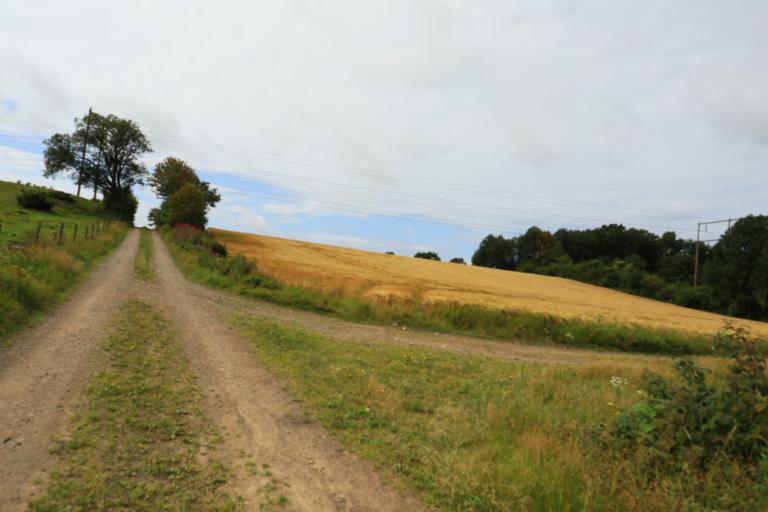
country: SE
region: Halland
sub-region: Varbergs Kommun
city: Traslovslage
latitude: 57.1217
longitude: 12.3246
